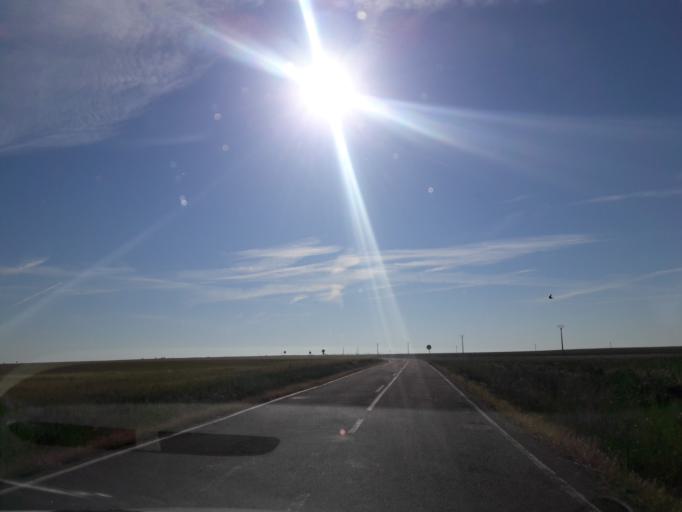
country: ES
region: Castille and Leon
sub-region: Provincia de Salamanca
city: Valdunciel
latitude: 41.0699
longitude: -5.6368
